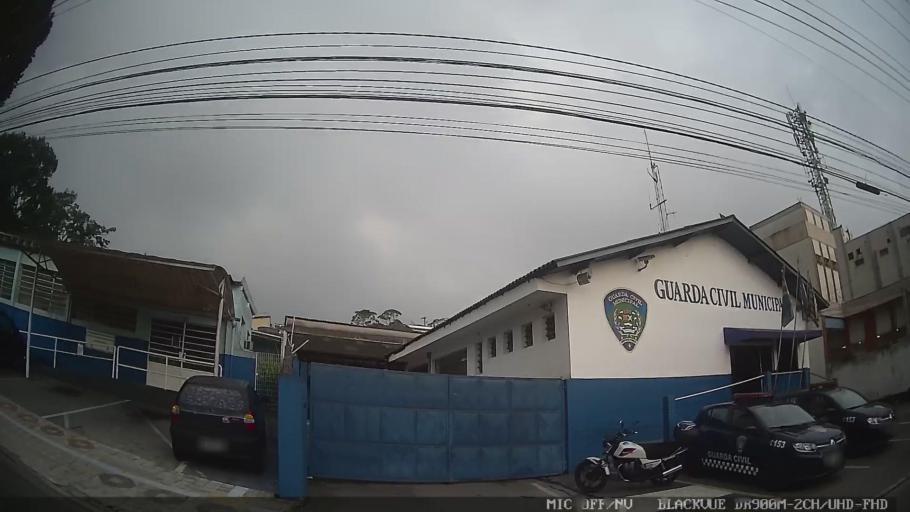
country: BR
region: Sao Paulo
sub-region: Ribeirao Pires
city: Ribeirao Pires
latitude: -23.7118
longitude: -46.4115
